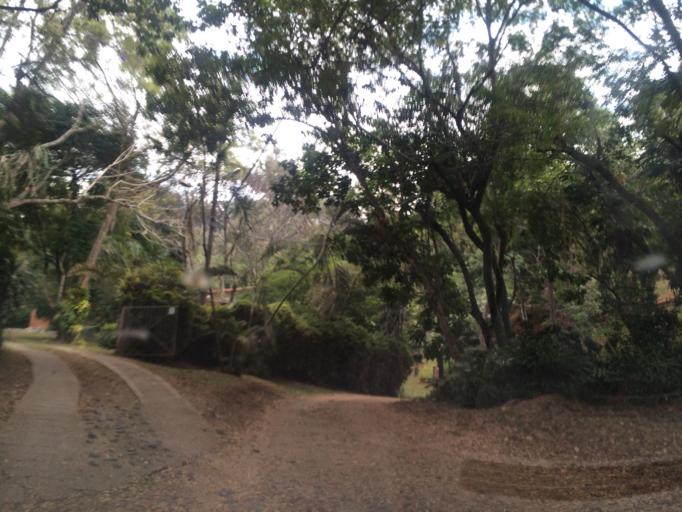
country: CO
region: Valle del Cauca
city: Cali
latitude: 3.4389
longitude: -76.5567
